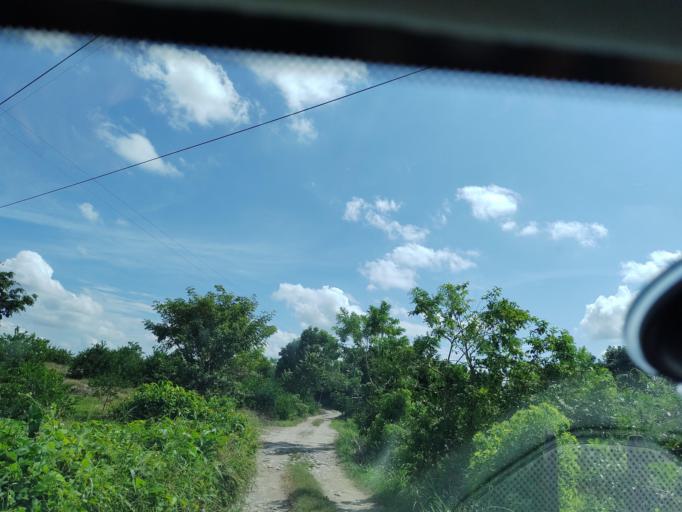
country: MX
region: Veracruz
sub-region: Martinez de la Torre
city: El Progreso
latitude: 20.1131
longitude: -97.0095
